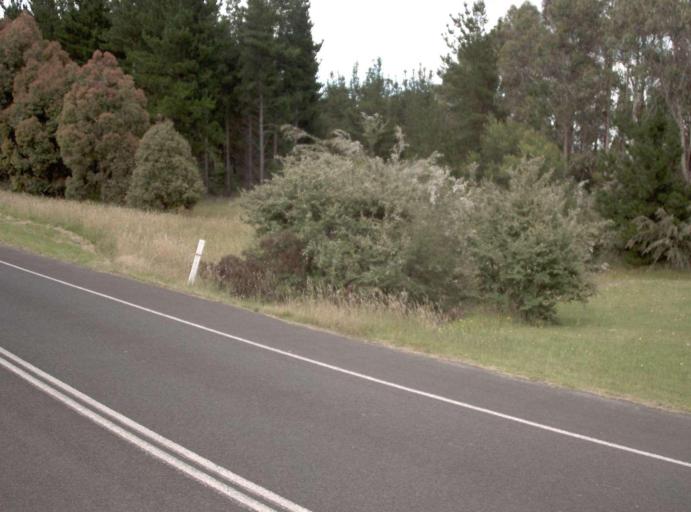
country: AU
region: Victoria
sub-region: Latrobe
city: Morwell
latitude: -38.1919
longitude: 146.4506
